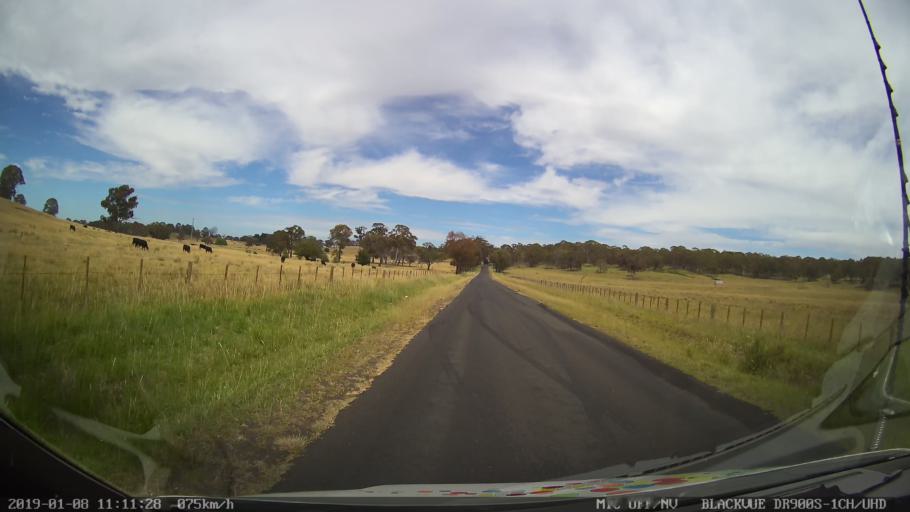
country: AU
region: New South Wales
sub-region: Guyra
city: Guyra
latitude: -30.2262
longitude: 151.6238
